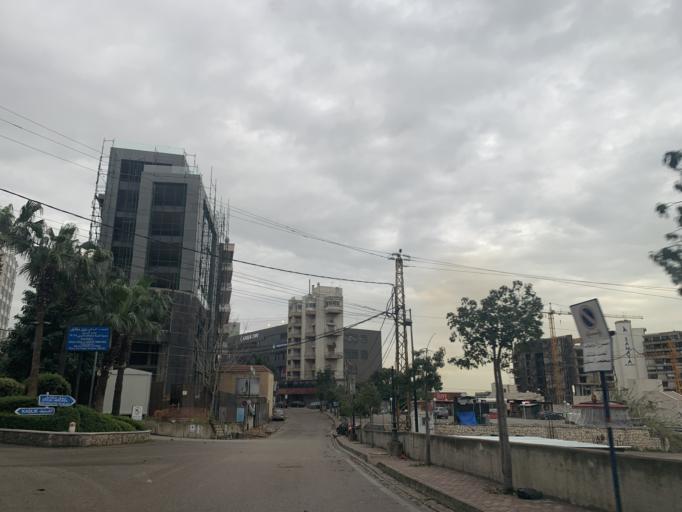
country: LB
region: Mont-Liban
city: Djounie
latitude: 33.9775
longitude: 35.6150
